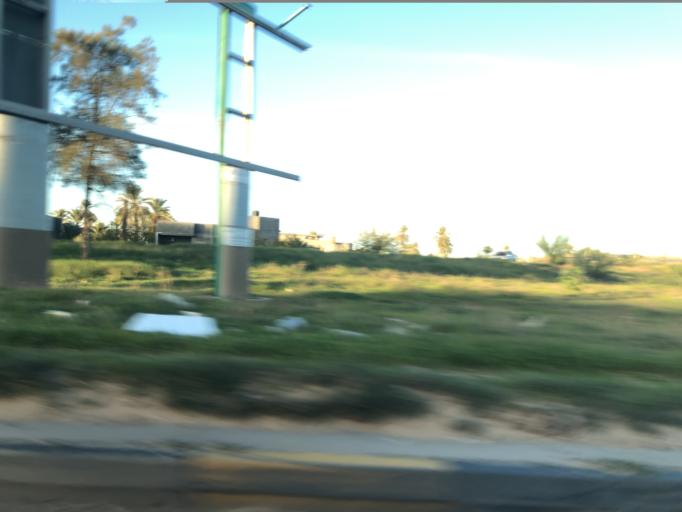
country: LY
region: Tripoli
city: Tagiura
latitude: 32.8693
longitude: 13.2871
